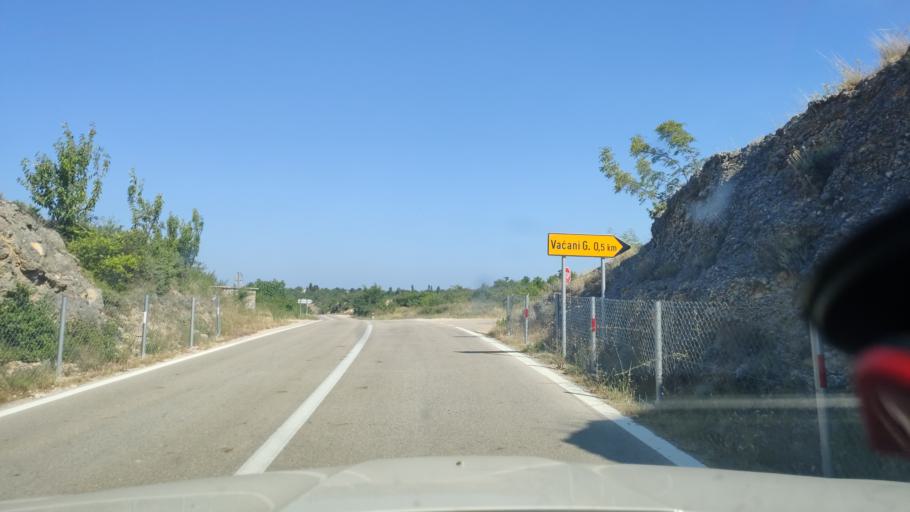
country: HR
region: Sibensko-Kniniska
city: Zaton
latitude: 43.9067
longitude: 15.8581
